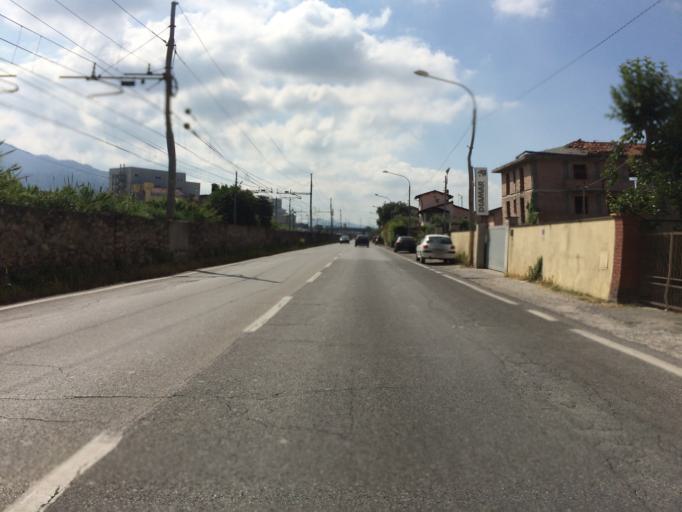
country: IT
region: Tuscany
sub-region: Provincia di Lucca
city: Strettoia
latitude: 43.9828
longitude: 10.1922
